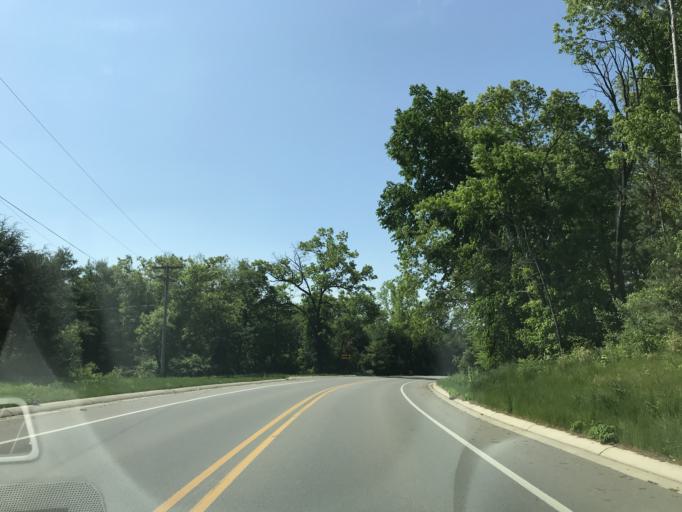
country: US
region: Michigan
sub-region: Oakland County
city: South Lyon
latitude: 42.4743
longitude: -83.6962
